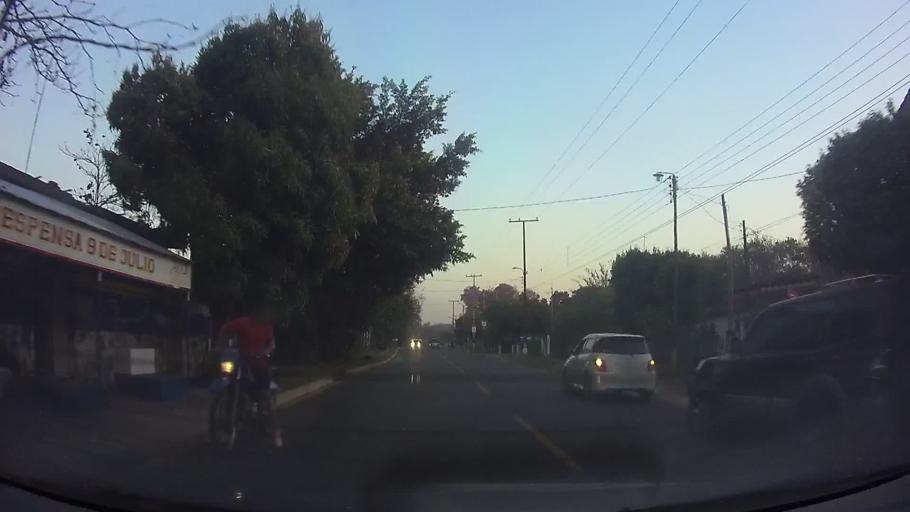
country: PY
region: Central
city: Limpio
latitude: -25.2394
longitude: -57.4910
